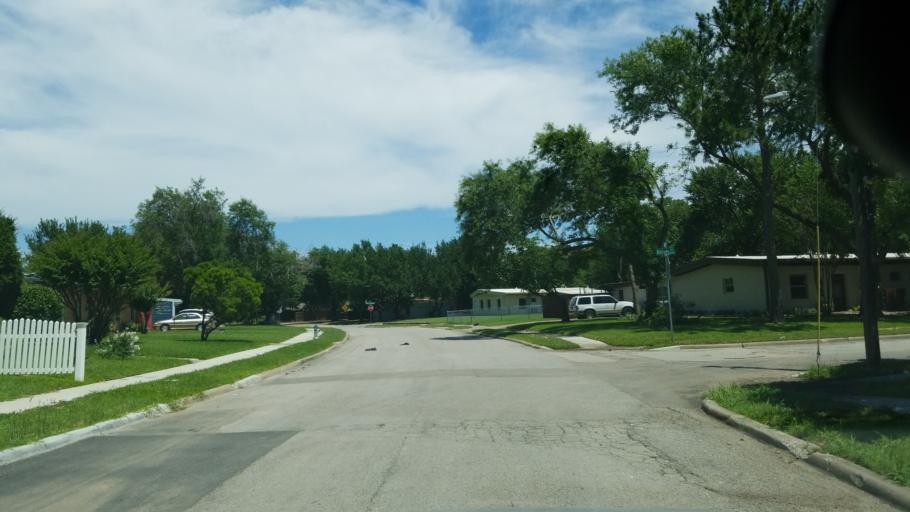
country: US
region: Texas
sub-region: Dallas County
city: Irving
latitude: 32.8323
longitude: -96.9694
